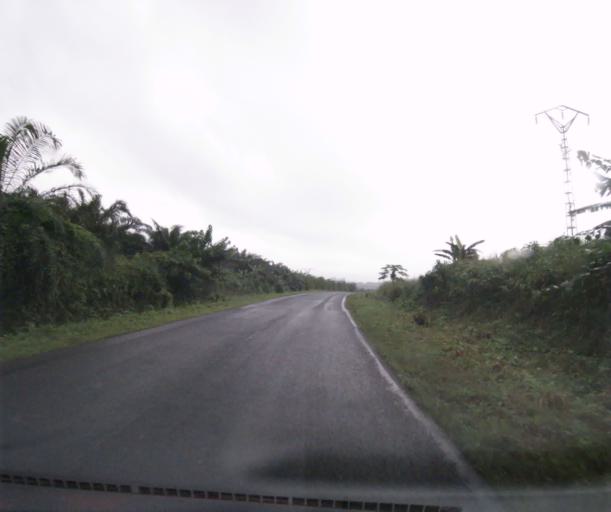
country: CM
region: South-West Province
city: Idenao
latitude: 4.1808
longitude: 9.0028
